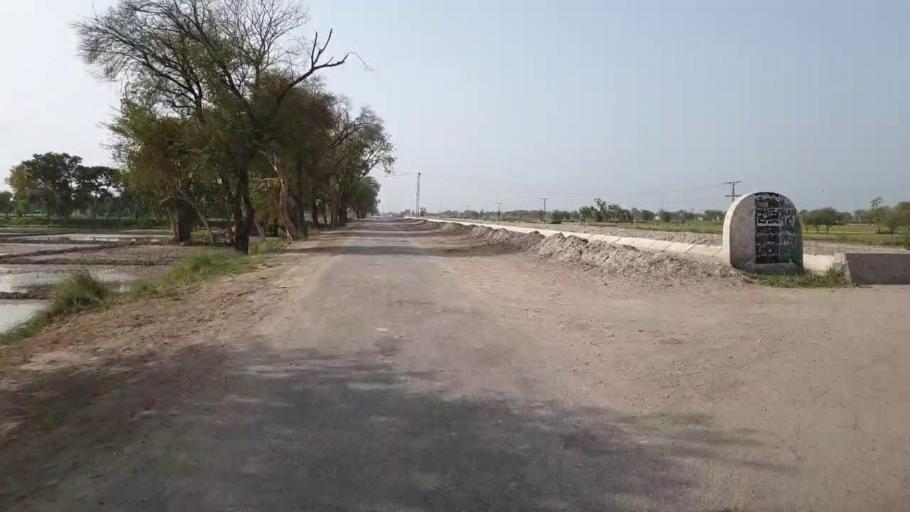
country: PK
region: Sindh
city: Daur
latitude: 26.3272
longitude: 68.1654
